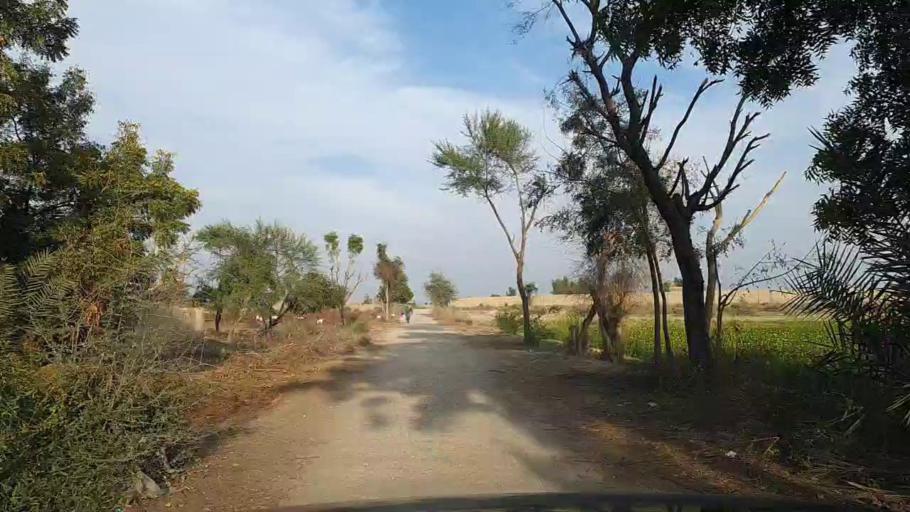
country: PK
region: Sindh
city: Jam Sahib
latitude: 26.4606
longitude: 68.5726
